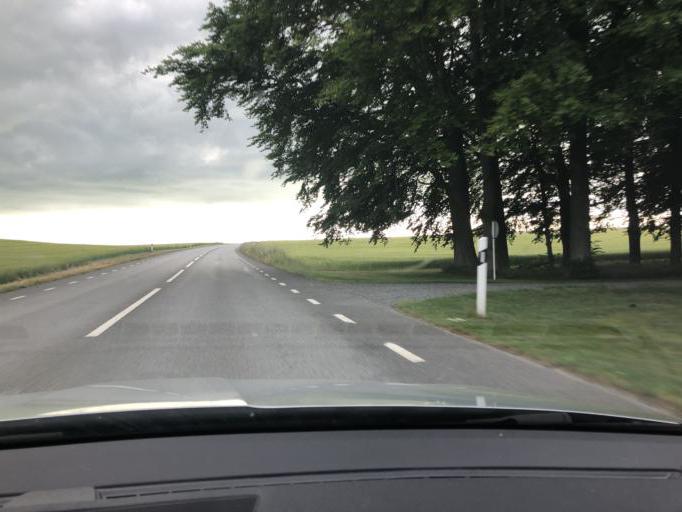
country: SE
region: Skane
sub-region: Simrishamns Kommun
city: Simrishamn
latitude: 55.5300
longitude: 14.2632
